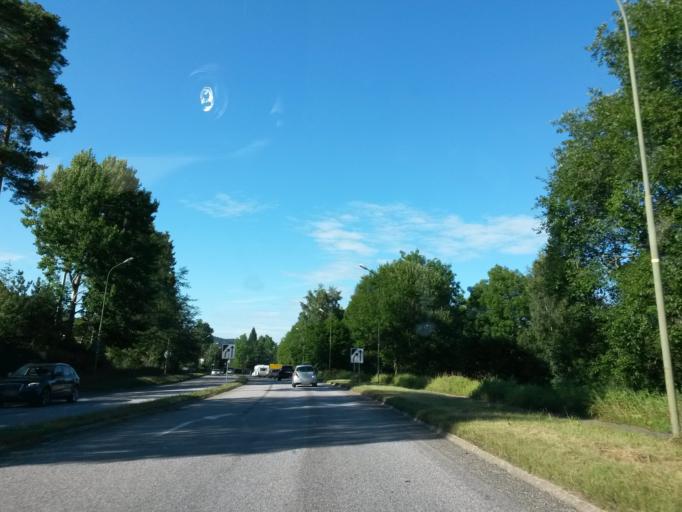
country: SE
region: Vaestra Goetaland
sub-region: Boras Kommun
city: Boras
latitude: 57.7566
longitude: 12.9521
